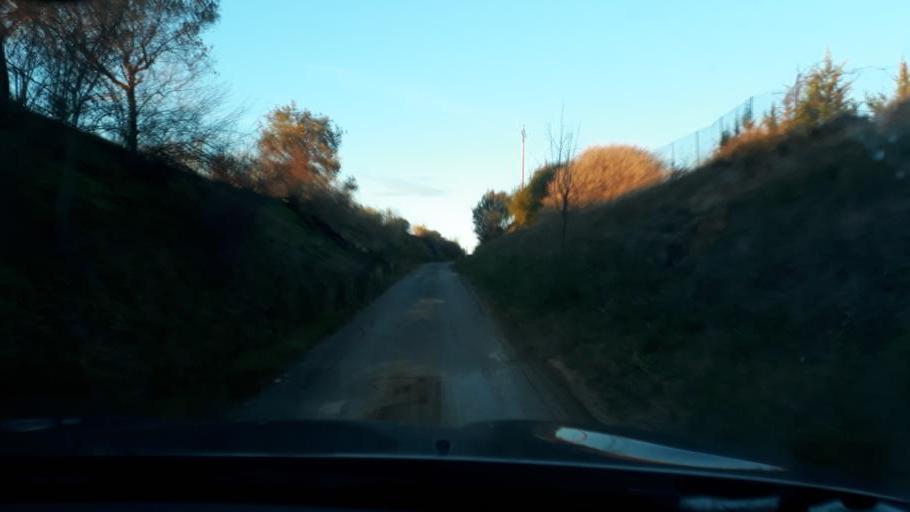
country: FR
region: Languedoc-Roussillon
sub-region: Departement de l'Herault
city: Florensac
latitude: 43.3971
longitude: 3.4593
